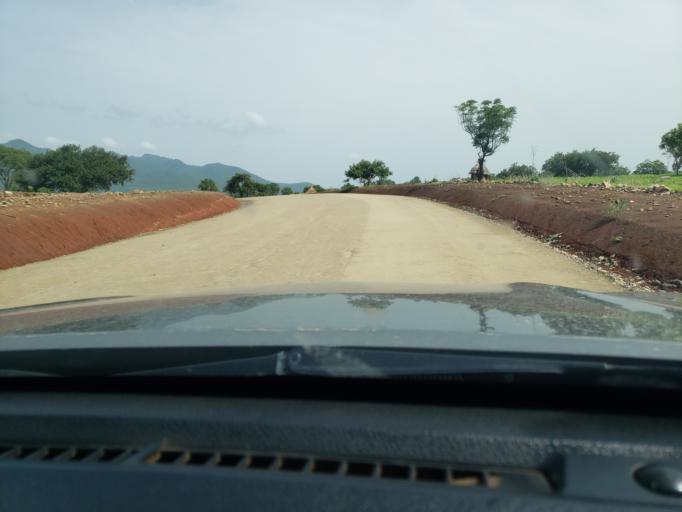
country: ET
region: Oromiya
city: Mendi
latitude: 10.1212
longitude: 35.1510
